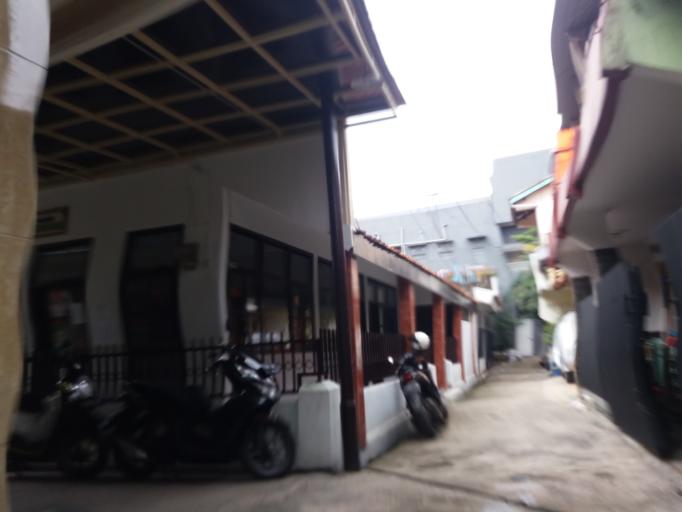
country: ID
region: West Java
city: Bandung
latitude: -6.9235
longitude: 107.6518
